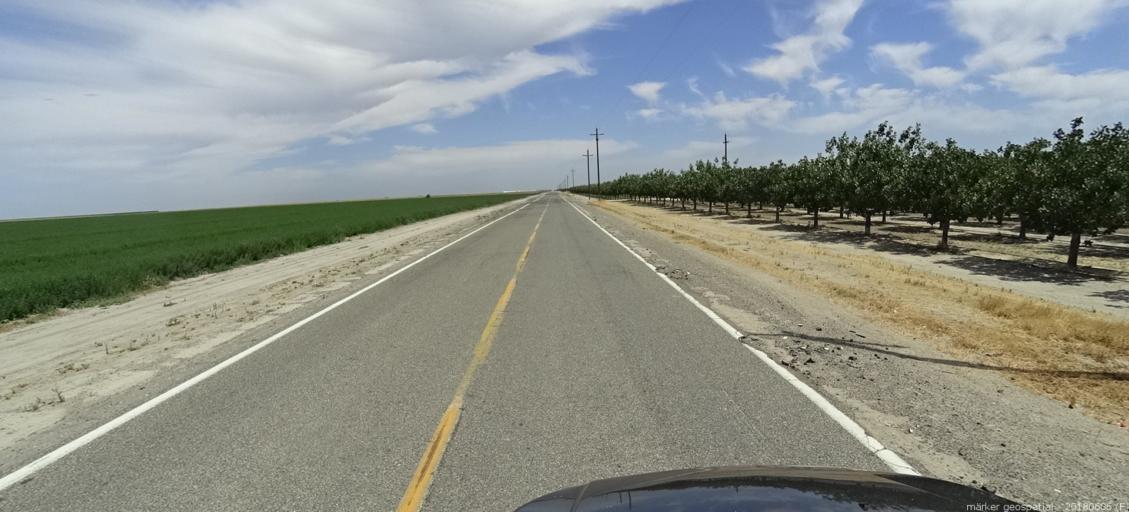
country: US
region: California
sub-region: Fresno County
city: Firebaugh
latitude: 36.8754
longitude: -120.3819
